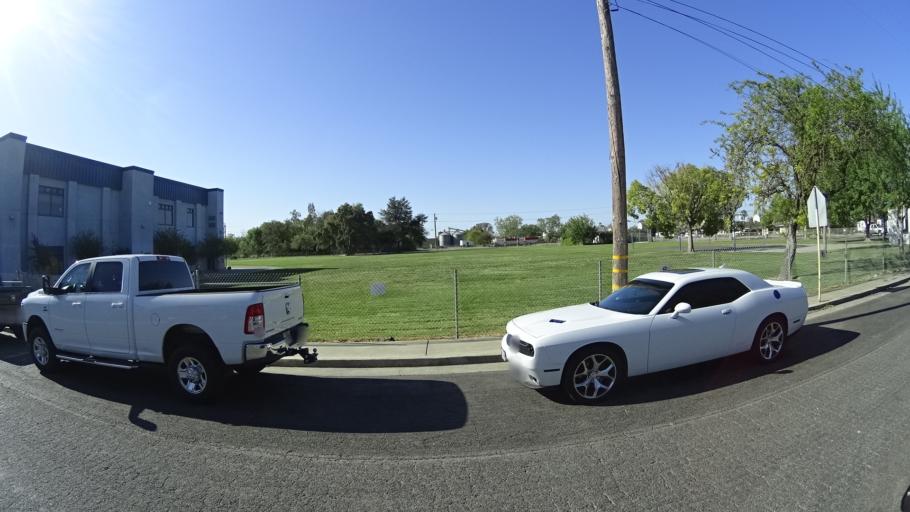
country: US
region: California
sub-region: Glenn County
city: Orland
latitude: 39.7416
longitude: -122.1942
